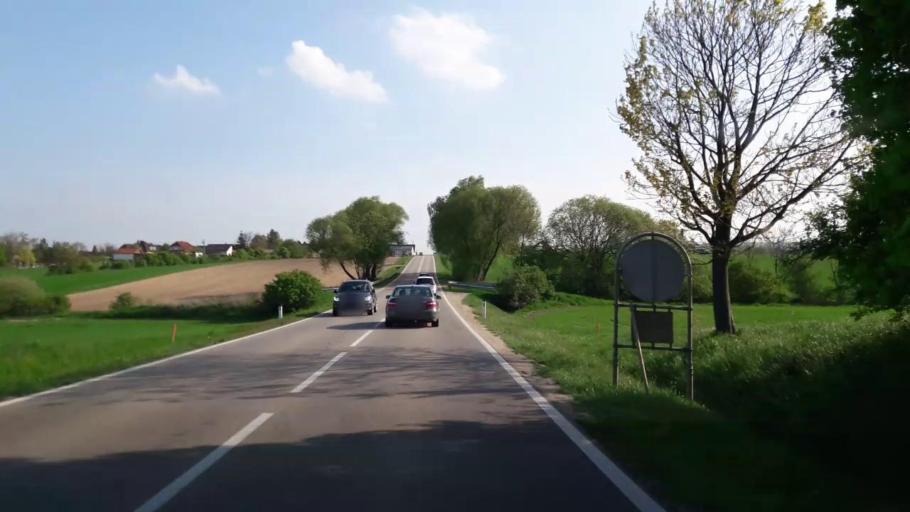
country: AT
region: Lower Austria
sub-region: Politischer Bezirk Hollabrunn
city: Wullersdorf
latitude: 48.6081
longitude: 16.0654
